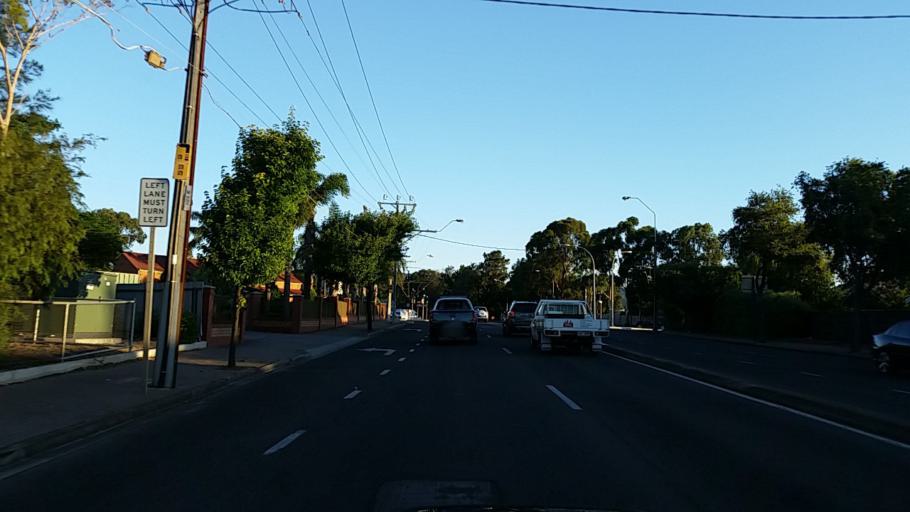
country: AU
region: South Australia
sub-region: Campbelltown
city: Paradise
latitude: -34.8756
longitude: 138.6706
